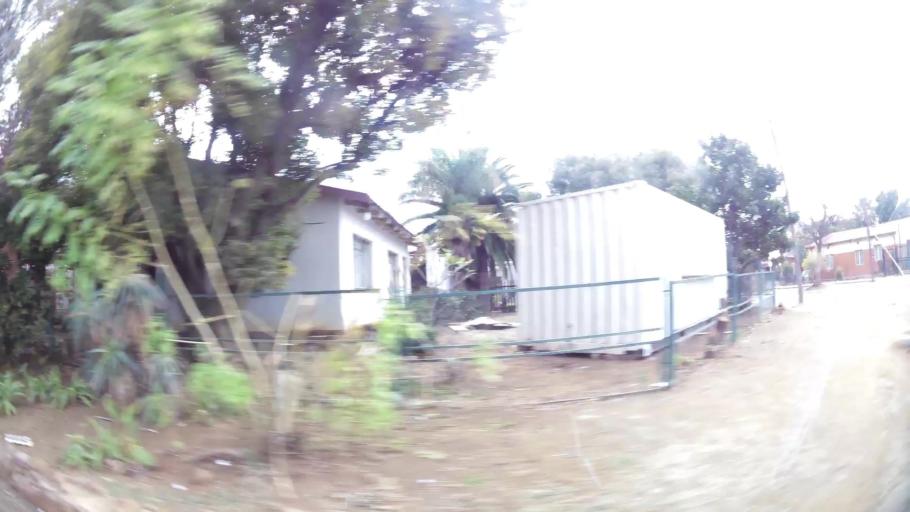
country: ZA
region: Gauteng
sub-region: City of Tshwane Metropolitan Municipality
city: Pretoria
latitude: -25.7154
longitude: 28.3209
